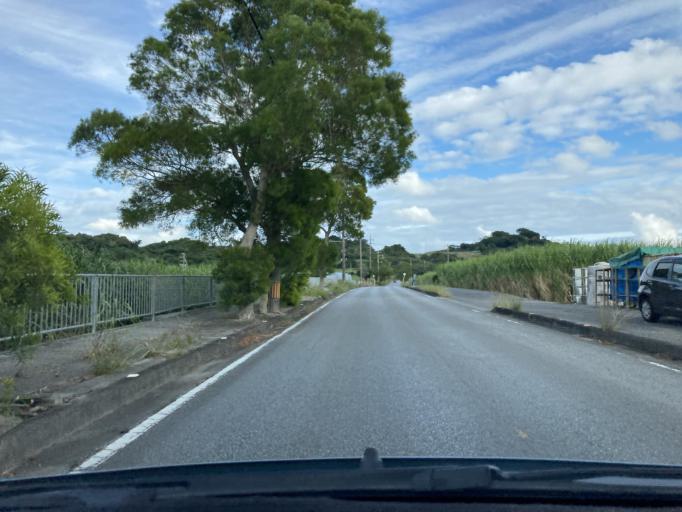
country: JP
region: Okinawa
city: Itoman
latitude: 26.1353
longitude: 127.7175
